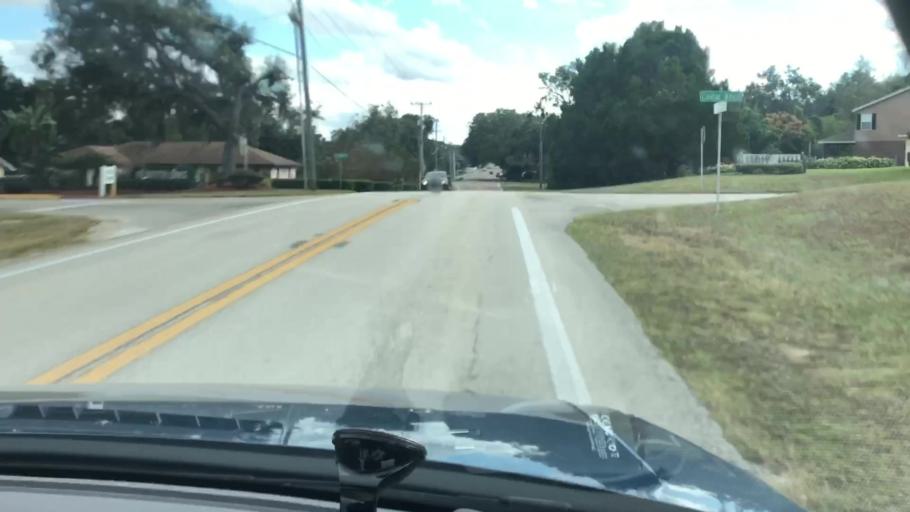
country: US
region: Florida
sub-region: Polk County
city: Gibsonia
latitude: 28.1314
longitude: -81.9384
